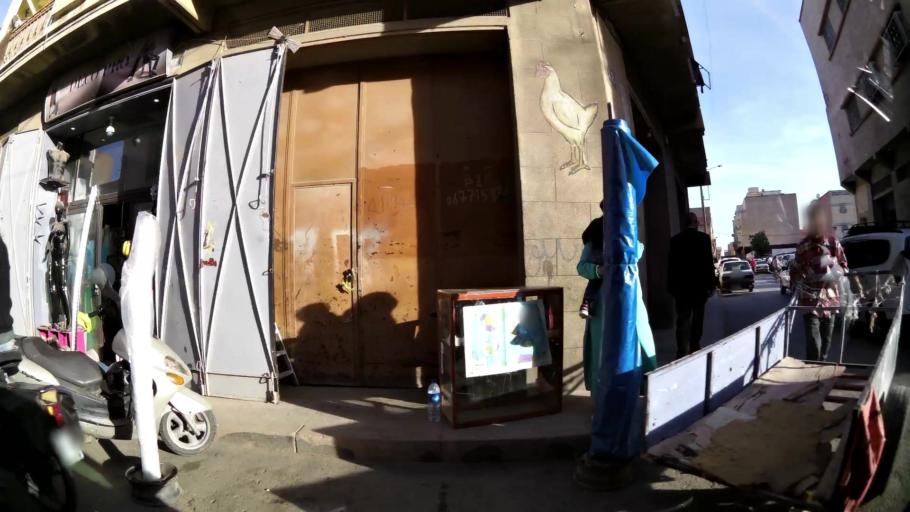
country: MA
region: Oriental
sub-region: Oujda-Angad
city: Oujda
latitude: 34.6784
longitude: -1.9088
